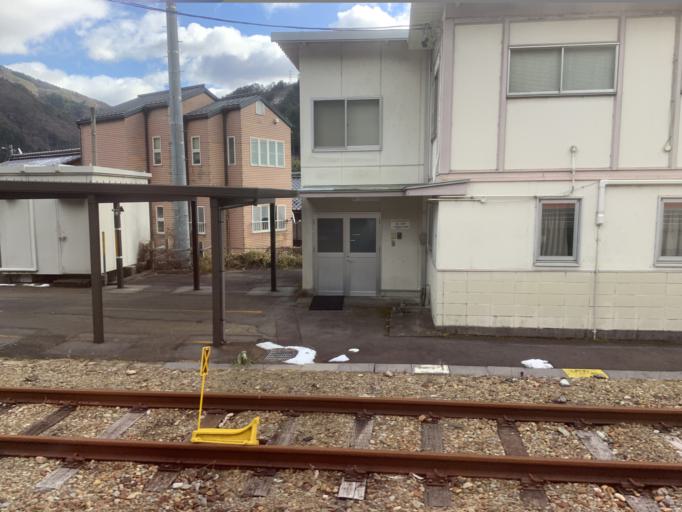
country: JP
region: Gifu
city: Takayama
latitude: 35.9501
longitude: 137.2563
